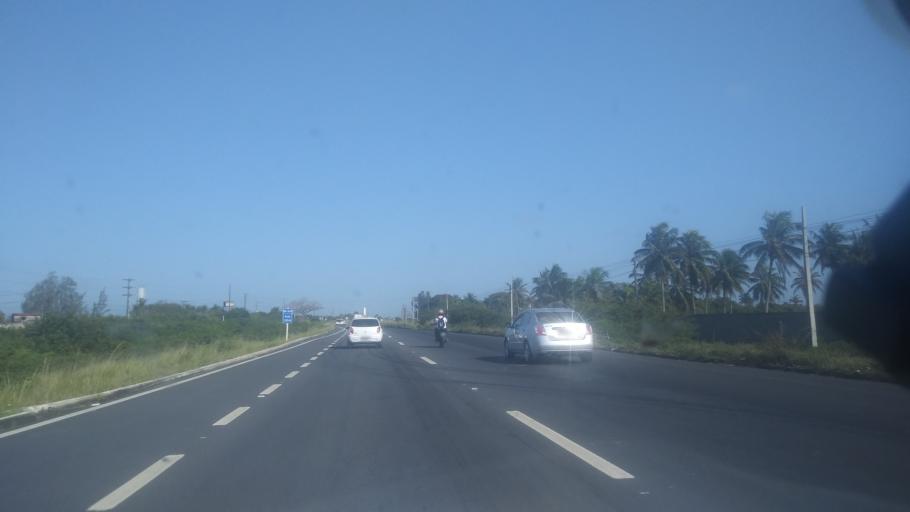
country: BR
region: Rio Grande do Norte
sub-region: Parnamirim
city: Parnamirim
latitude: -5.8851
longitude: -35.2802
